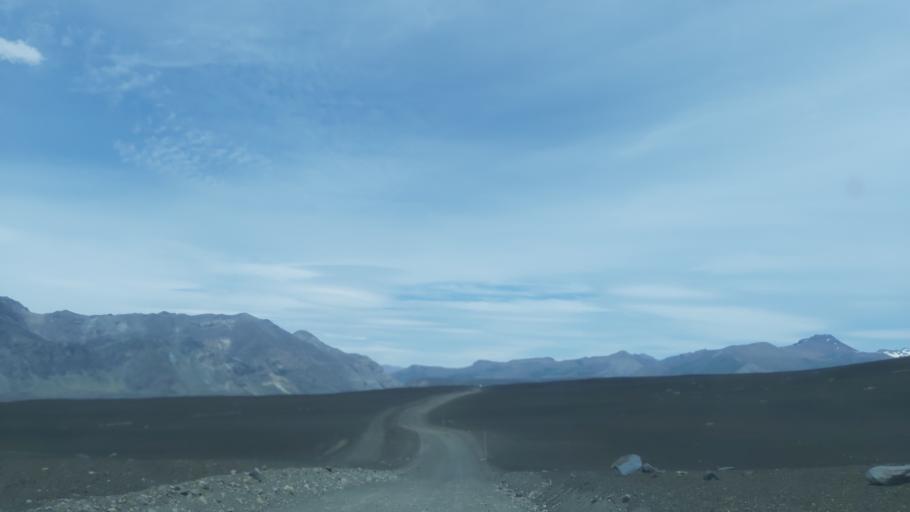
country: AR
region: Neuquen
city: Andacollo
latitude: -37.4285
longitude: -71.2867
